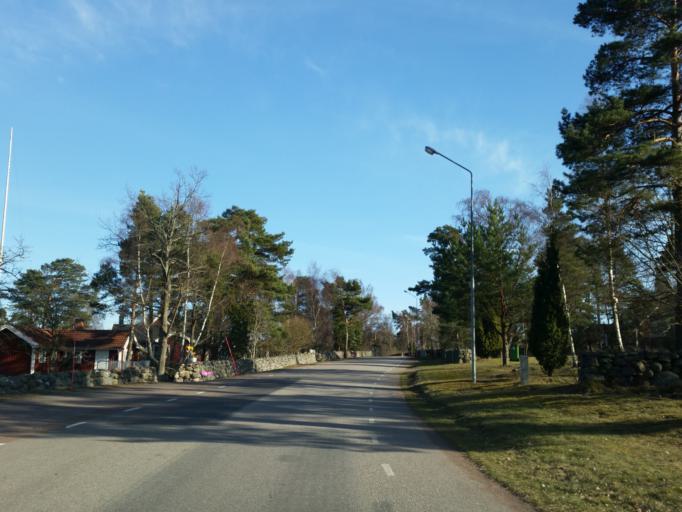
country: SE
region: Kalmar
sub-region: Kalmar Kommun
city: Lindsdal
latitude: 56.7809
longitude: 16.4101
